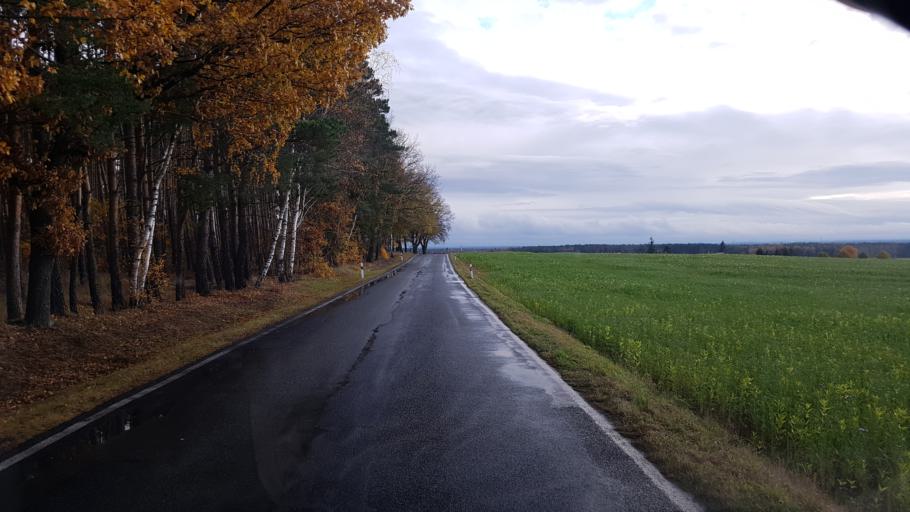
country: DE
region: Saxony
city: Thiendorf
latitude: 51.3252
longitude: 13.7409
